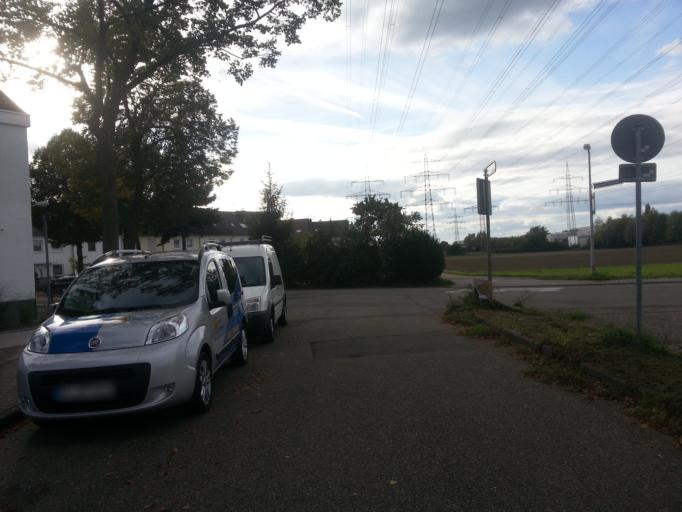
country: DE
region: Rheinland-Pfalz
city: Altrip
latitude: 49.4483
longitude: 8.5249
